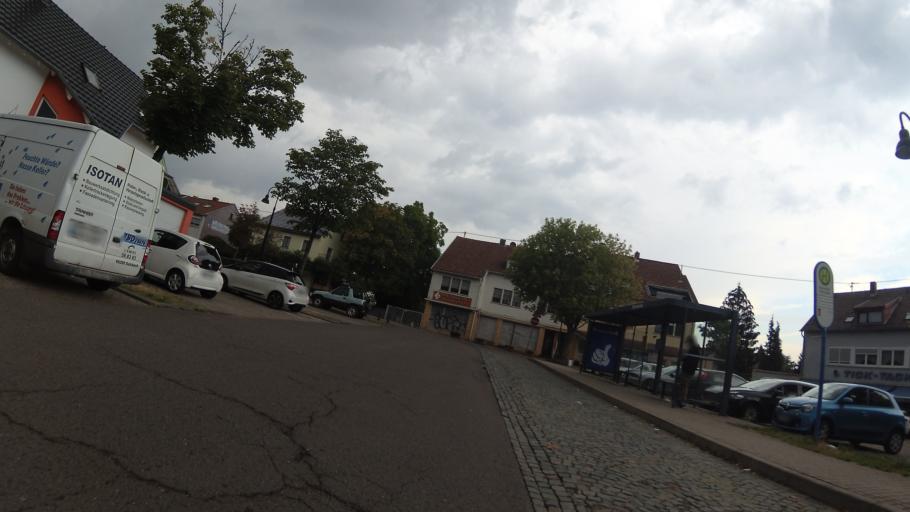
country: DE
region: Saarland
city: Sulzbach
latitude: 49.2858
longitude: 7.0746
